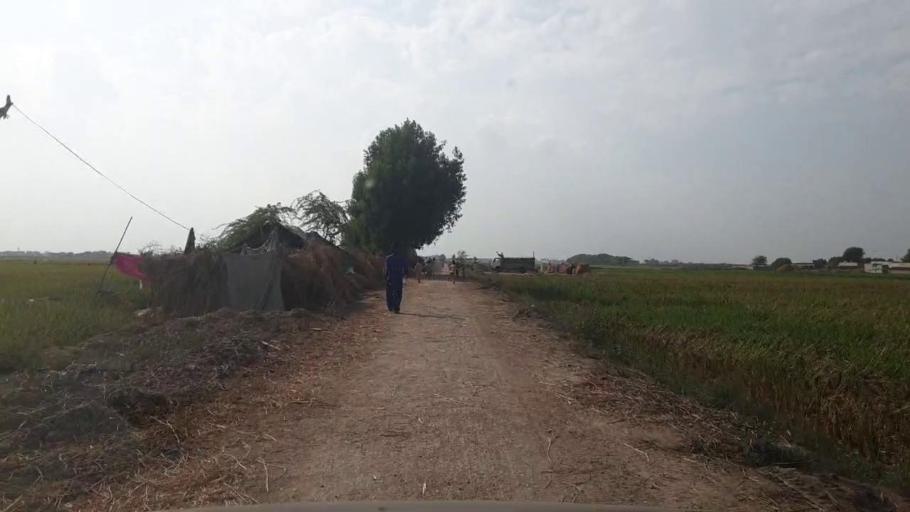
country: PK
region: Sindh
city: Kario
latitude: 24.6345
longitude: 68.5568
